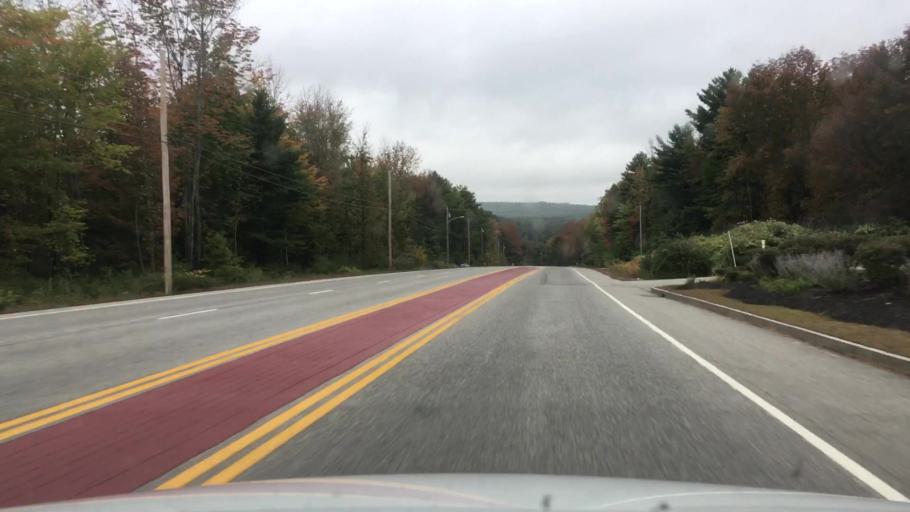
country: US
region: Maine
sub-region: Androscoggin County
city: Poland
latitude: 44.0313
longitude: -70.3681
